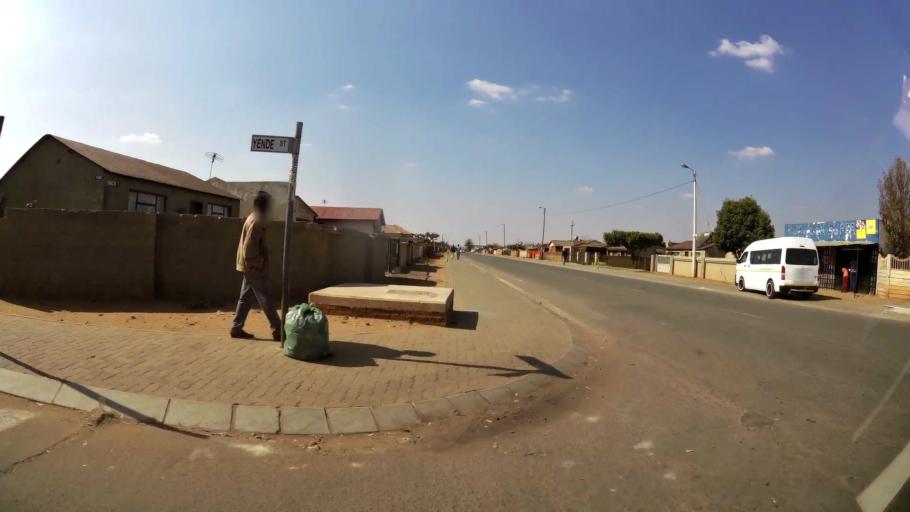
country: ZA
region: Gauteng
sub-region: Ekurhuleni Metropolitan Municipality
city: Benoni
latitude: -26.1493
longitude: 28.4050
